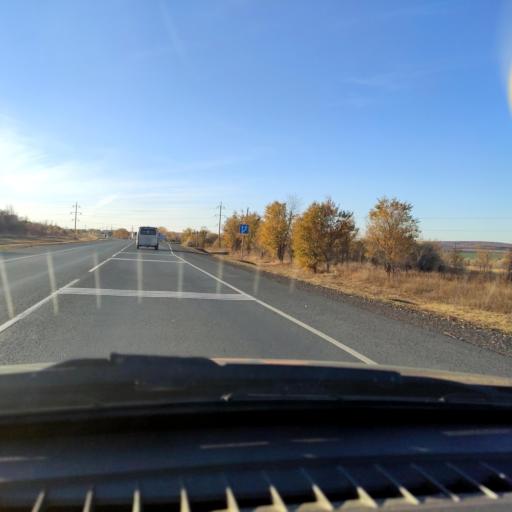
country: RU
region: Samara
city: Varlamovo
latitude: 53.1935
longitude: 48.3323
